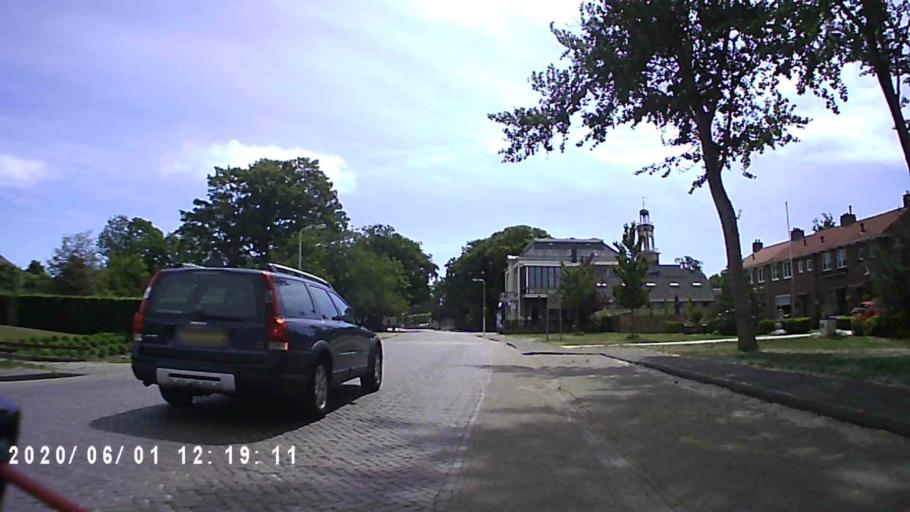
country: NL
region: Friesland
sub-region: Gemeente Harlingen
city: Harlingen
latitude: 53.1310
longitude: 5.4740
